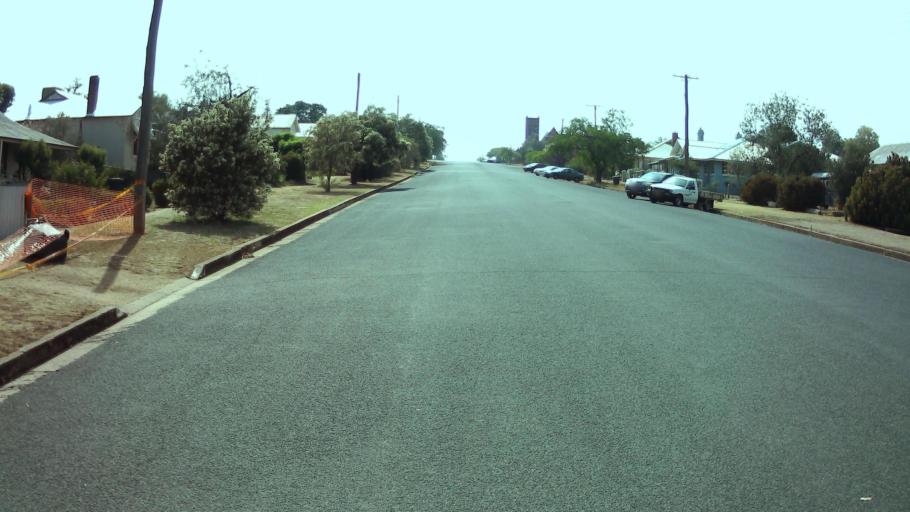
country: AU
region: New South Wales
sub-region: Weddin
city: Grenfell
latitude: -33.8957
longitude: 148.1579
